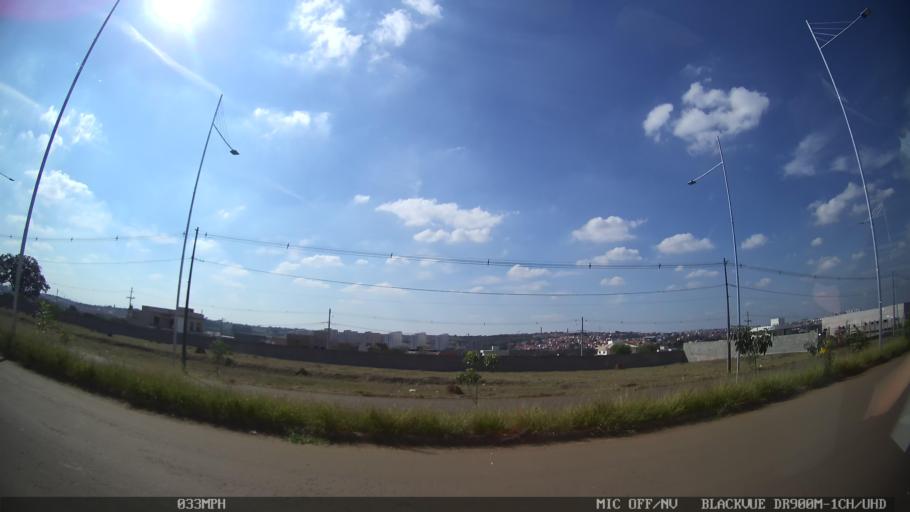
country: BR
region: Sao Paulo
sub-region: Hortolandia
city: Hortolandia
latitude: -22.8651
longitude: -47.2323
